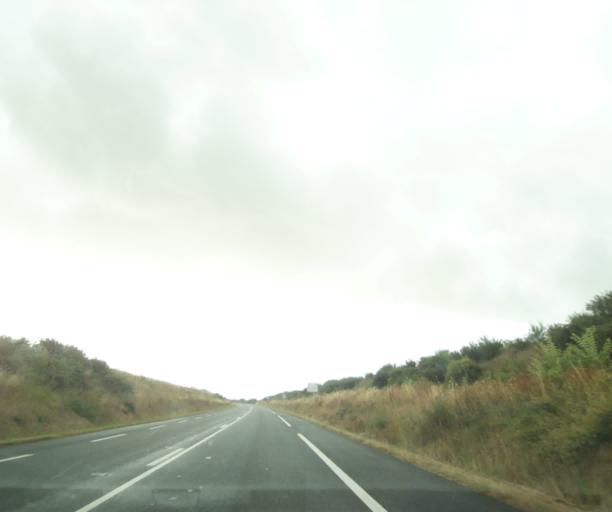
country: FR
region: Pays de la Loire
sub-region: Departement de la Vendee
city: Saint-Hilaire-de-Talmont
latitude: 46.4664
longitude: -1.6437
